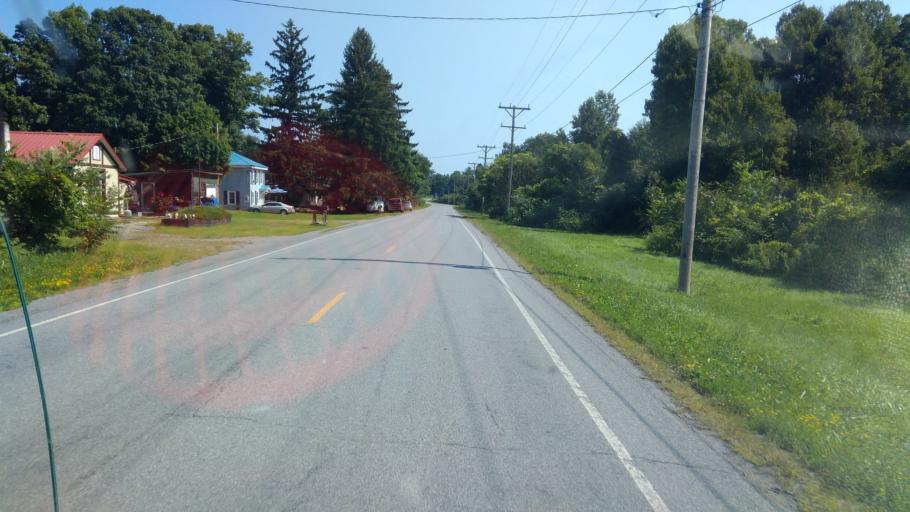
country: US
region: New York
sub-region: Allegany County
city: Belmont
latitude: 42.2488
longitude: -78.0692
